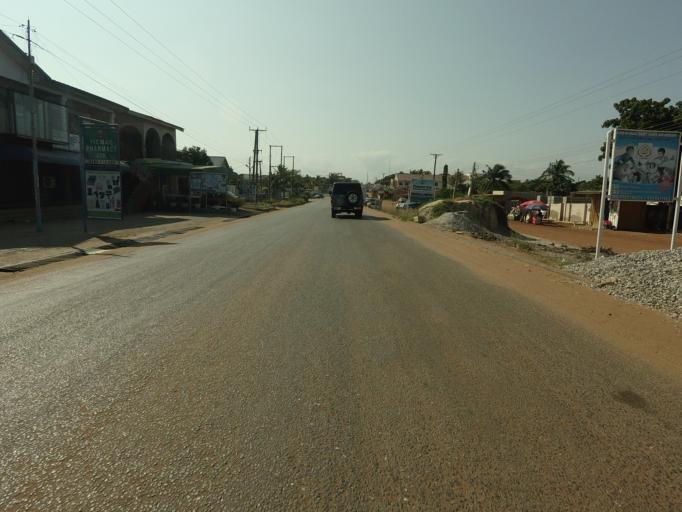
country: GH
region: Greater Accra
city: Teshi Old Town
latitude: 5.6006
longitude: -0.1035
